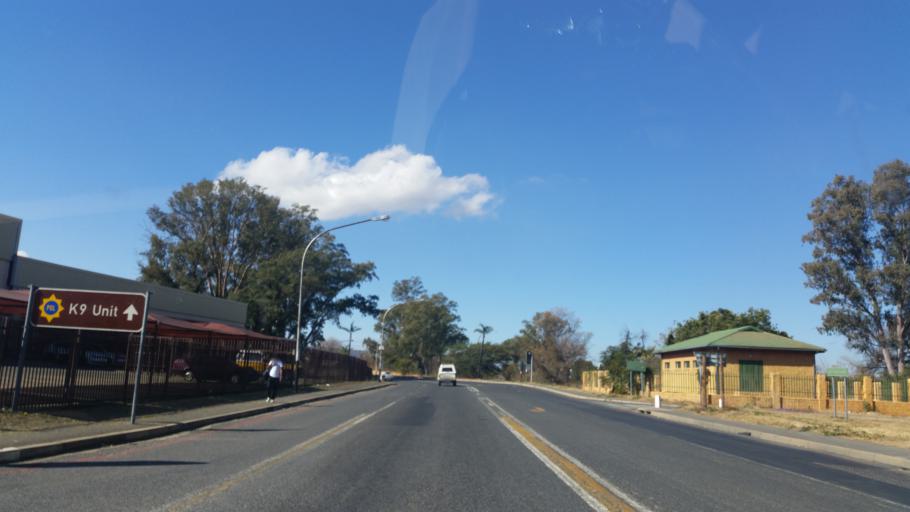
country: ZA
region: KwaZulu-Natal
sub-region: uThukela District Municipality
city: Ladysmith
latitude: -28.5688
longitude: 29.7742
